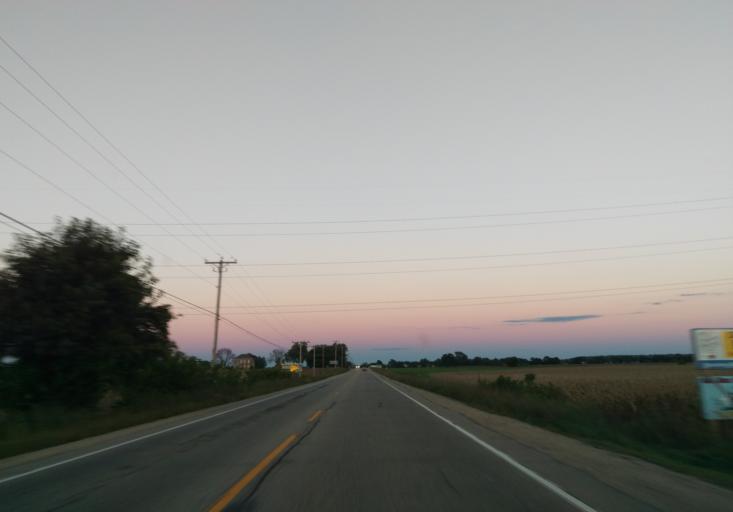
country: US
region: Wisconsin
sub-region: Rock County
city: Janesville
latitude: 42.7304
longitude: -89.1186
